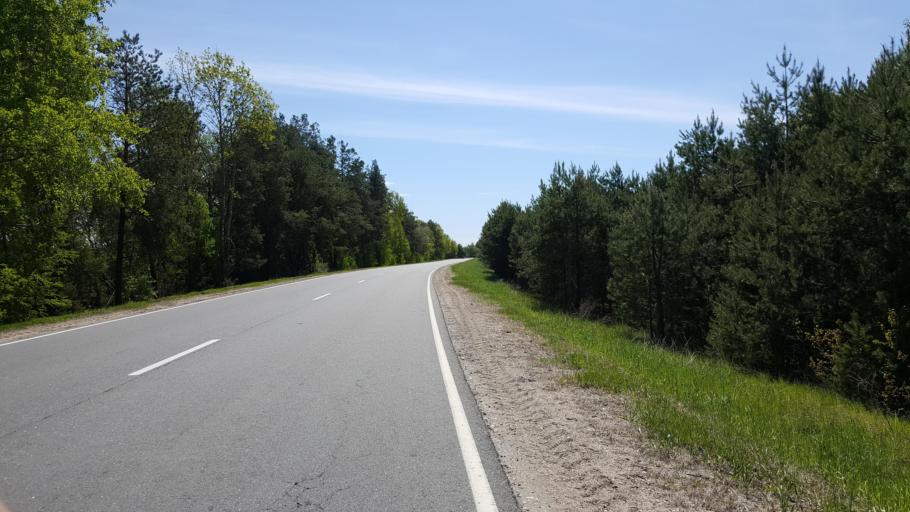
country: BY
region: Brest
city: Zhabinka
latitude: 52.3715
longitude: 24.1383
